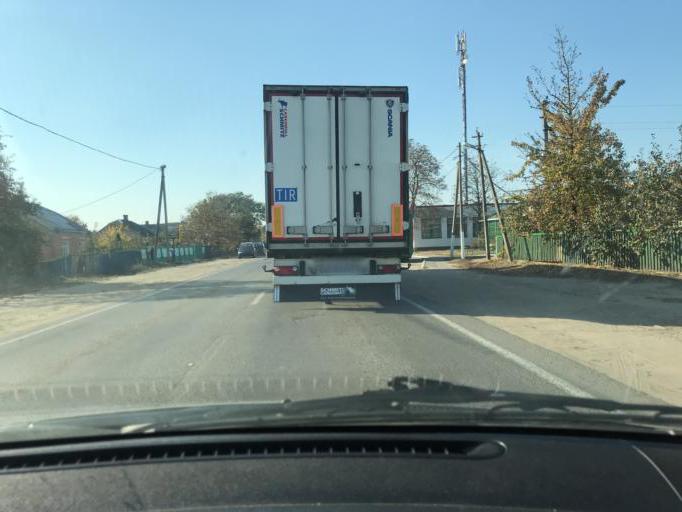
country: BY
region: Brest
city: Davyd-Haradok
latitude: 52.0764
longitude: 27.3518
